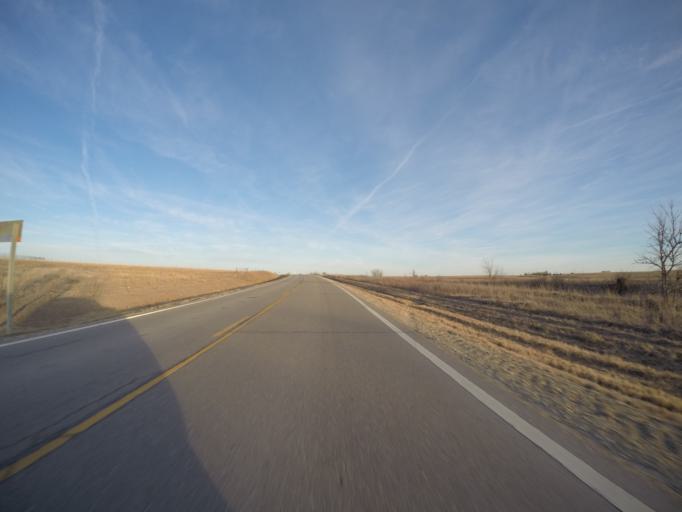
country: US
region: Kansas
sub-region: Dickinson County
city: Herington
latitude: 38.6605
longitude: -96.8555
